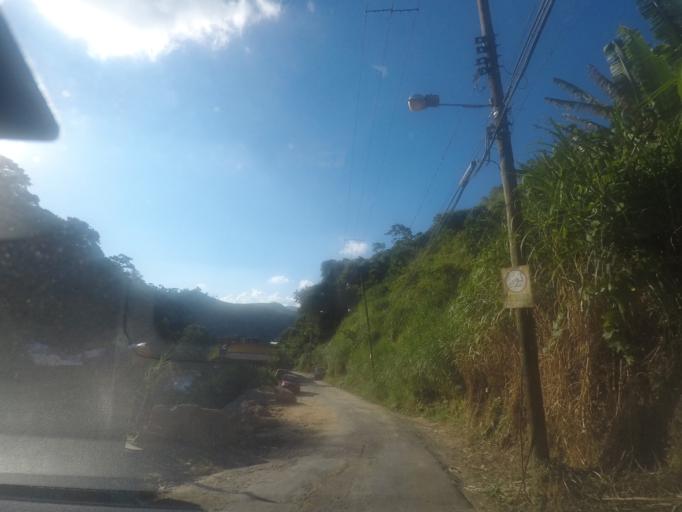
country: BR
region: Rio de Janeiro
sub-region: Petropolis
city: Petropolis
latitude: -22.5006
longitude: -43.1442
